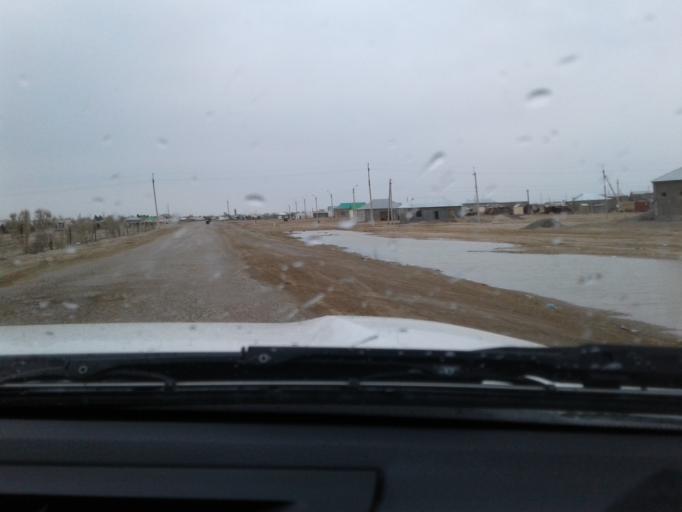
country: TM
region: Ahal
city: Abadan
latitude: 38.7549
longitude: 58.4903
